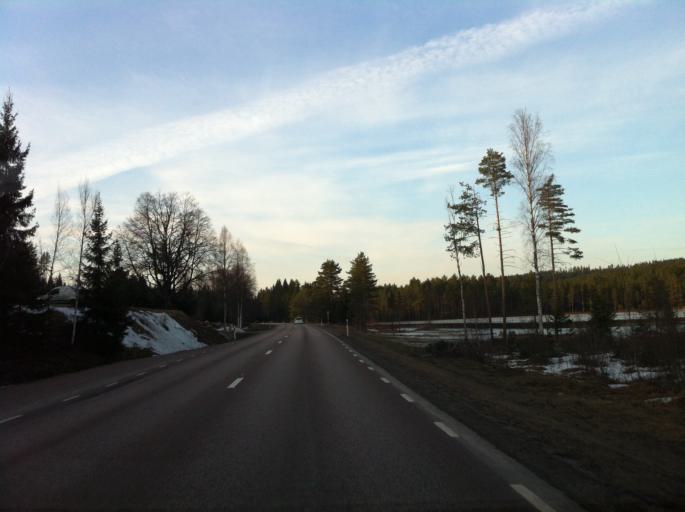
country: SE
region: Vaermland
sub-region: Filipstads Kommun
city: Lesjofors
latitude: 59.9458
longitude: 14.2133
